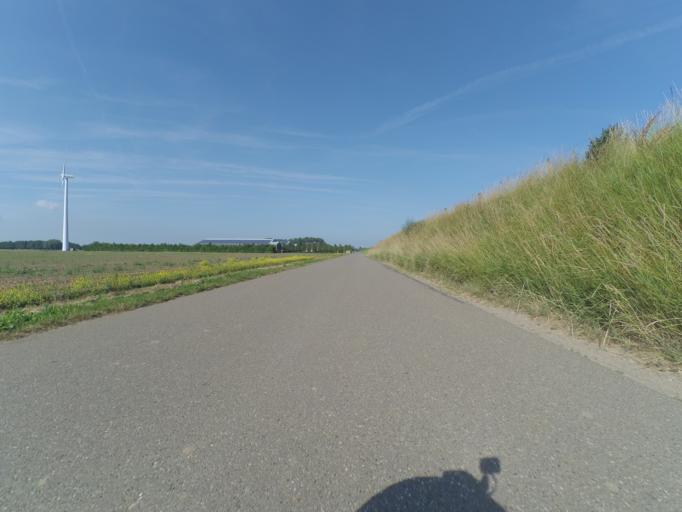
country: NL
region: North Brabant
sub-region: Gemeente Woensdrecht
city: Woensdrecht
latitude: 51.4289
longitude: 4.2940
